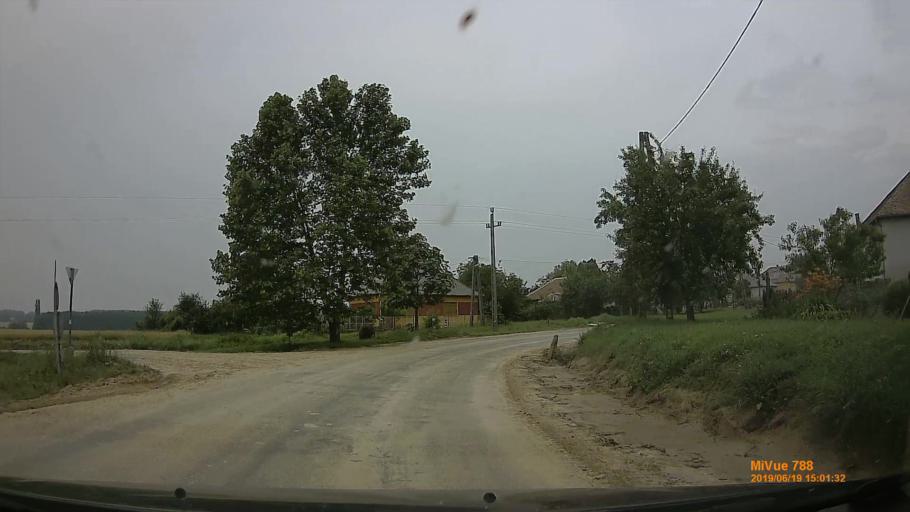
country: HU
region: Baranya
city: Szigetvar
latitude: 46.0872
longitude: 17.7980
